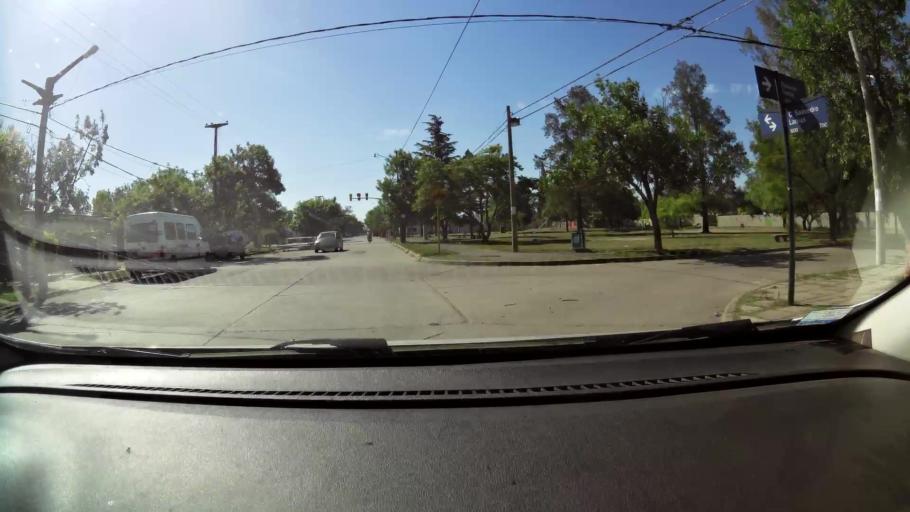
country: AR
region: Cordoba
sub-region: Departamento de Capital
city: Cordoba
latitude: -31.3648
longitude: -64.1680
